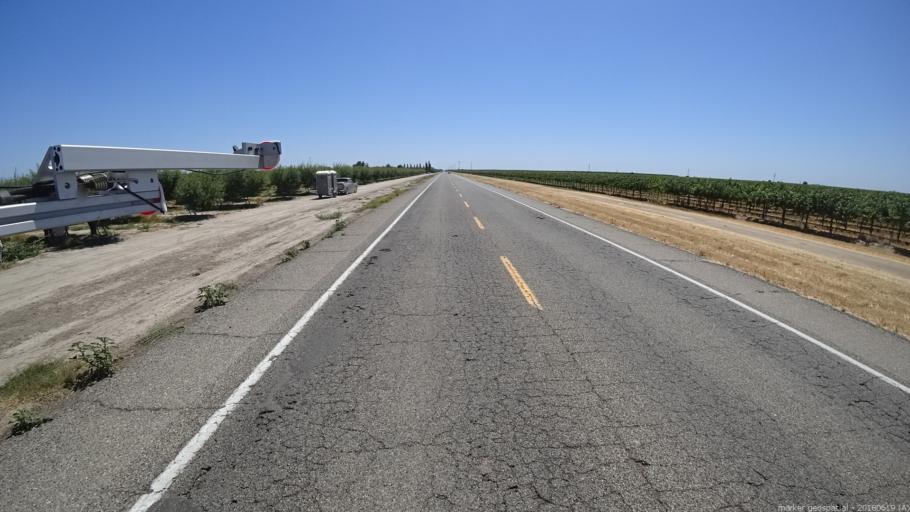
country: US
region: California
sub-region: Madera County
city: Parkwood
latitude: 36.8511
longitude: -120.2135
